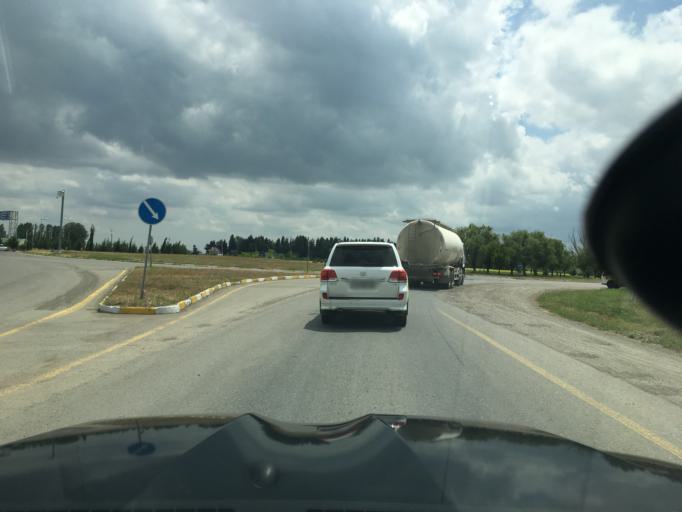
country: AZ
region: Tovuz
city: Qaraxanli
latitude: 41.0299
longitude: 45.5983
